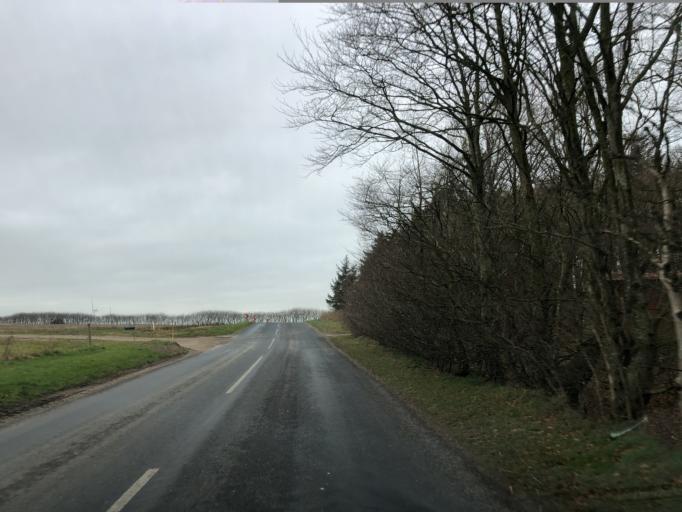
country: DK
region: Central Jutland
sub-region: Viborg Kommune
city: Stoholm
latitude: 56.4399
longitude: 9.1065
